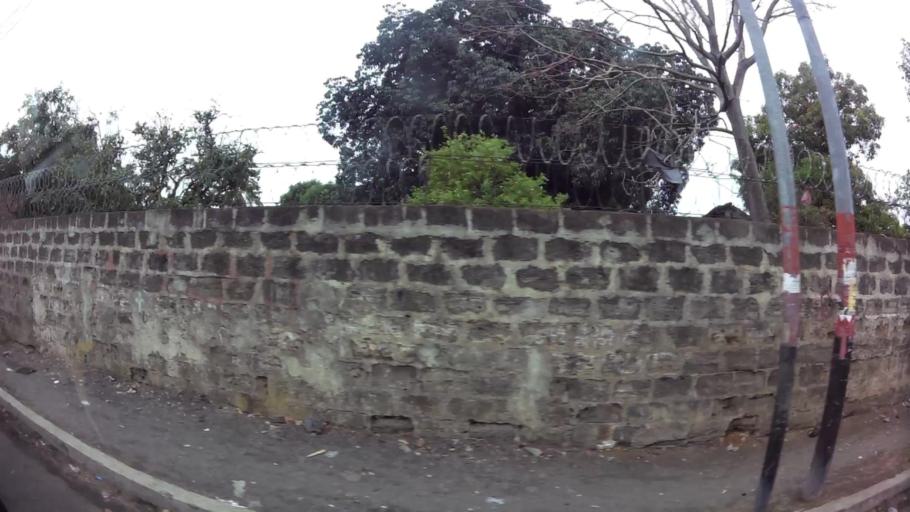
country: NI
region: Leon
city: Leon
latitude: 12.4397
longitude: -86.8718
